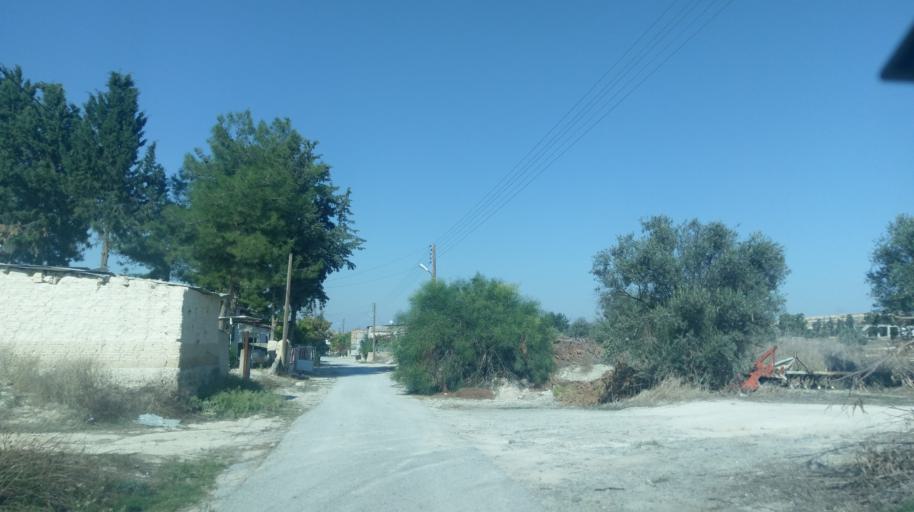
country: CY
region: Lefkosia
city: Lympia
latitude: 35.0062
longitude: 33.4644
